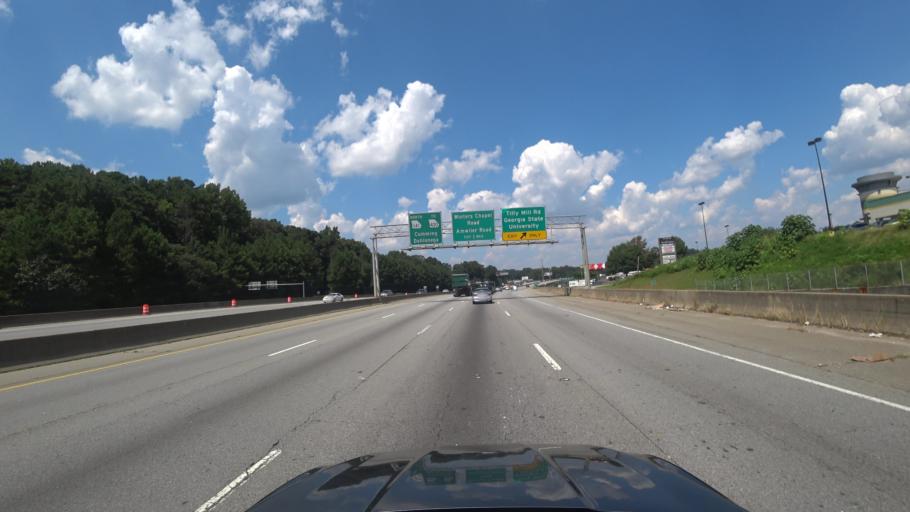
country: US
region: Georgia
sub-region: DeKalb County
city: Doraville
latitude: 33.9192
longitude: -84.2838
